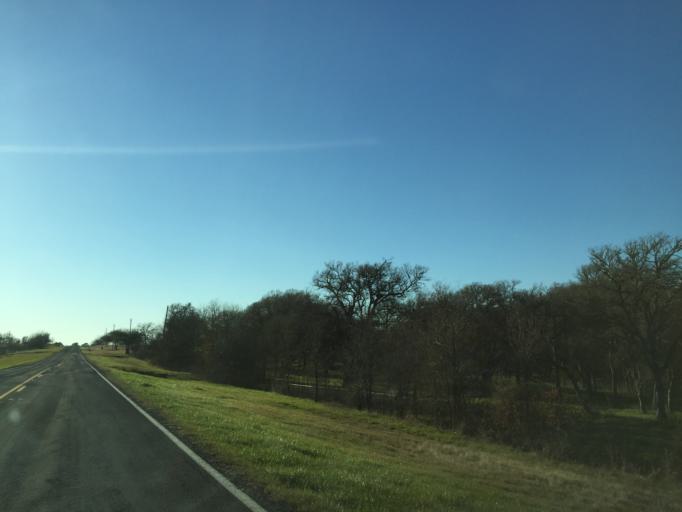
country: US
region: Texas
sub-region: Bastrop County
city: Elgin
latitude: 30.3613
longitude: -97.3308
